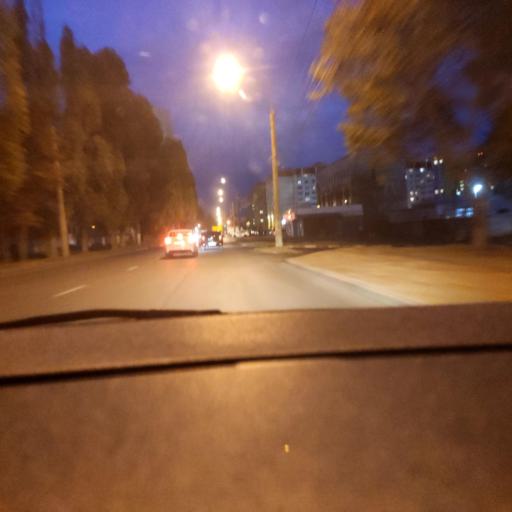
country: RU
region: Voronezj
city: Podgornoye
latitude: 51.6933
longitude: 39.1407
